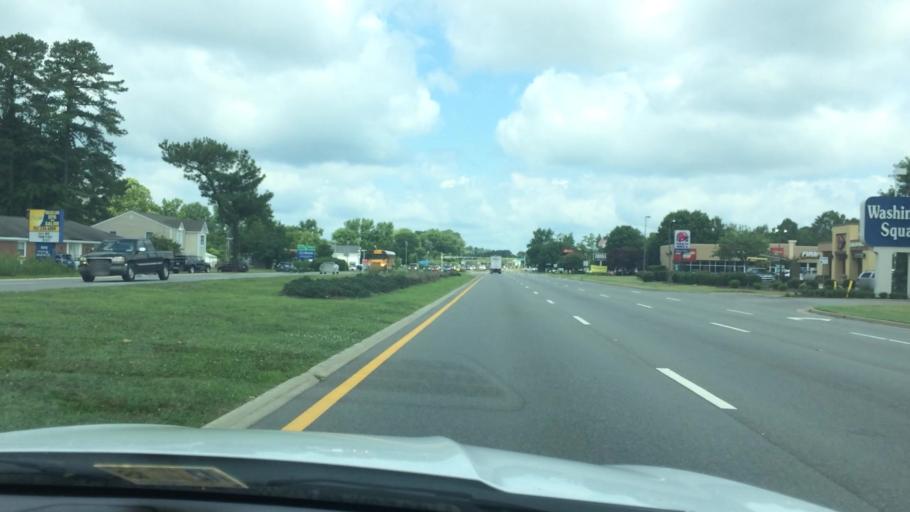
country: US
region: Virginia
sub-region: York County
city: Yorktown
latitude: 37.1568
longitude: -76.4623
